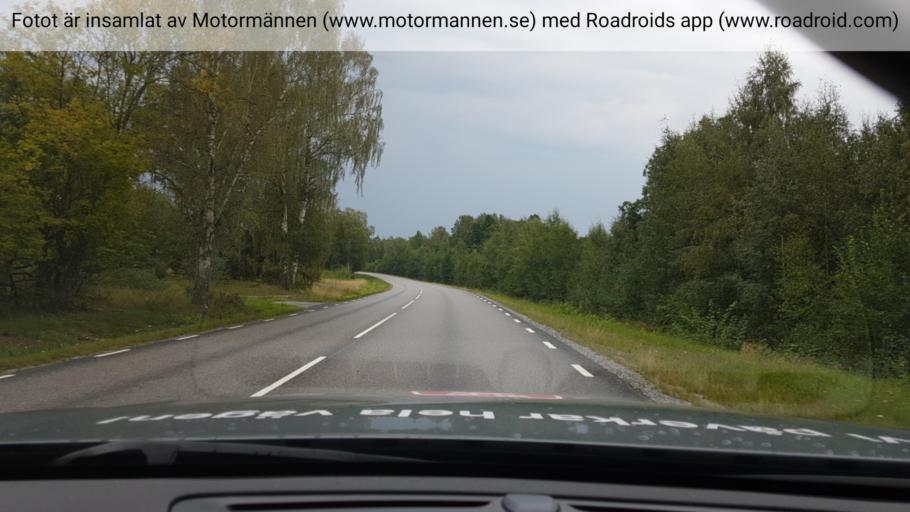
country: SE
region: Stockholm
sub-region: Upplands-Bro Kommun
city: Bro
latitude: 59.5289
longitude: 17.5793
